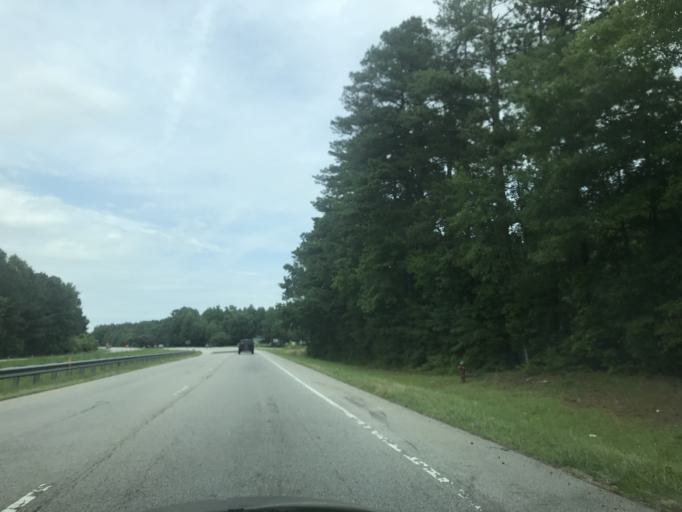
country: US
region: North Carolina
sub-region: Franklin County
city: Franklinton
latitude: 36.1138
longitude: -78.4563
